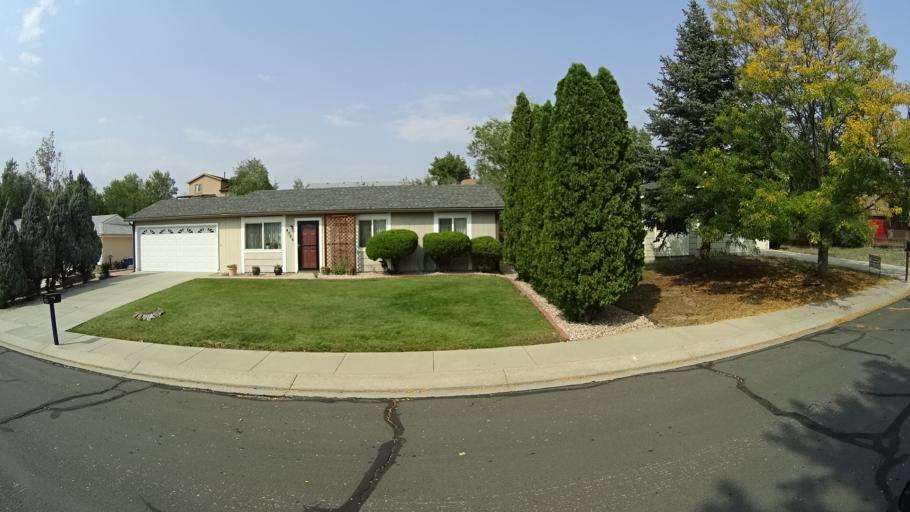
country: US
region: Colorado
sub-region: El Paso County
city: Cimarron Hills
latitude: 38.8310
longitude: -104.7438
